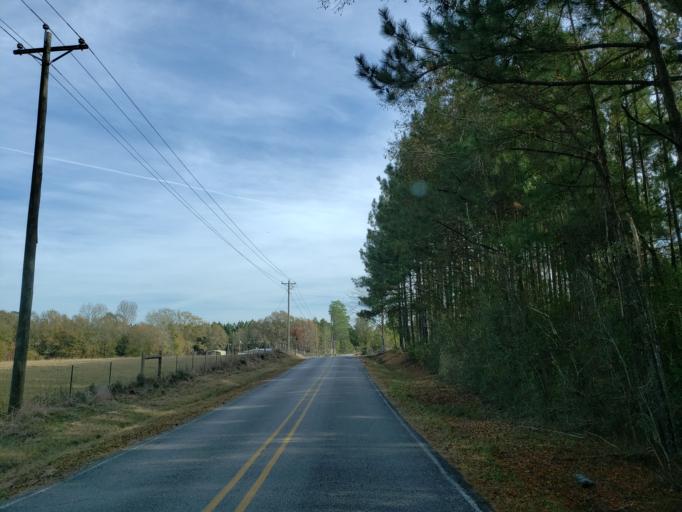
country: US
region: Mississippi
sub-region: Forrest County
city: Rawls Springs
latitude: 31.4139
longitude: -89.4149
